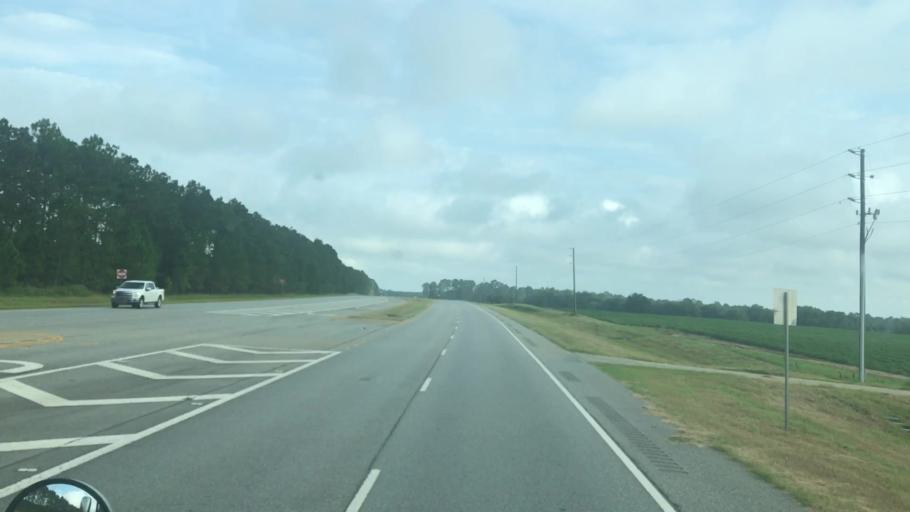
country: US
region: Georgia
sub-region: Miller County
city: Colquitt
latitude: 31.2048
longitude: -84.7713
